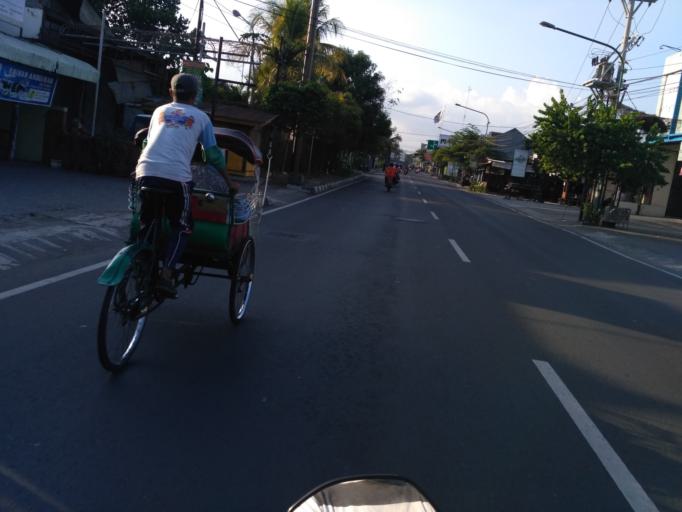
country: ID
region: Daerah Istimewa Yogyakarta
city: Yogyakarta
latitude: -7.8275
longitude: 110.3900
